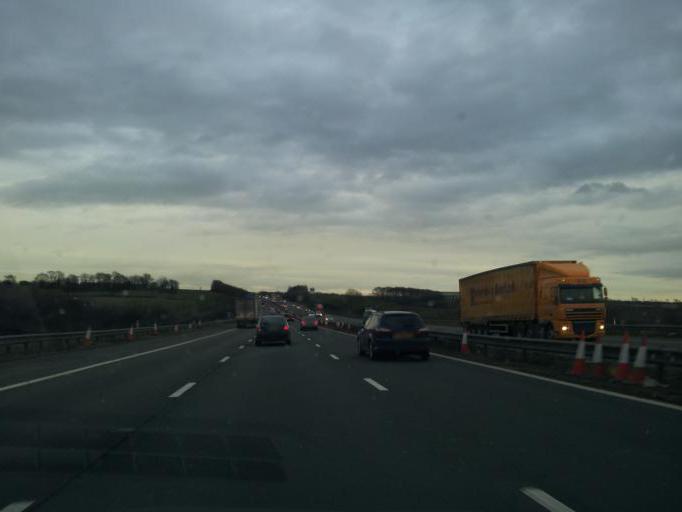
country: GB
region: England
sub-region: Warwickshire
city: Rugby
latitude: 52.4108
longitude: -1.2647
